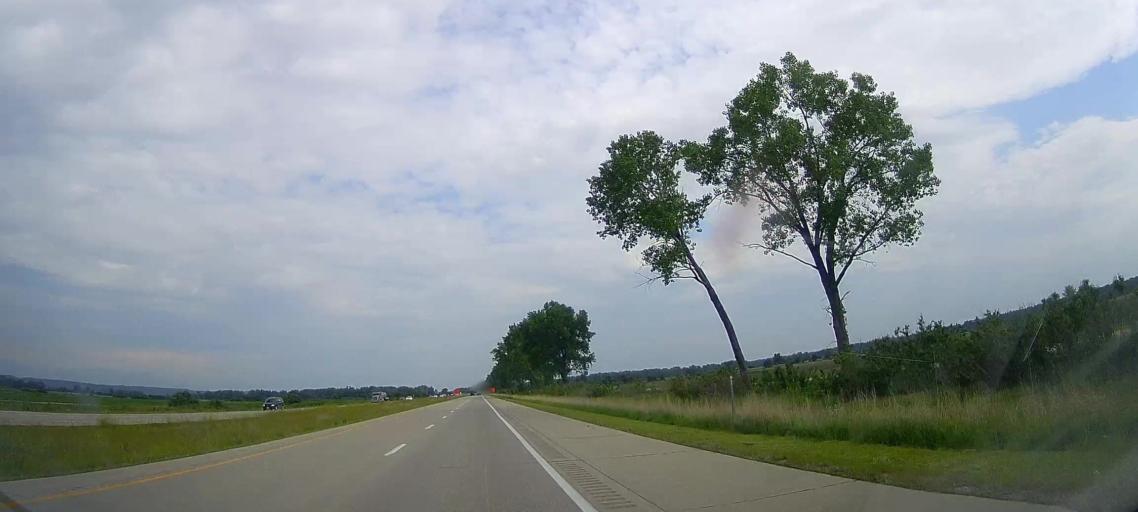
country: US
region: Nebraska
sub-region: Burt County
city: Tekamah
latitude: 41.8325
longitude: -96.0822
